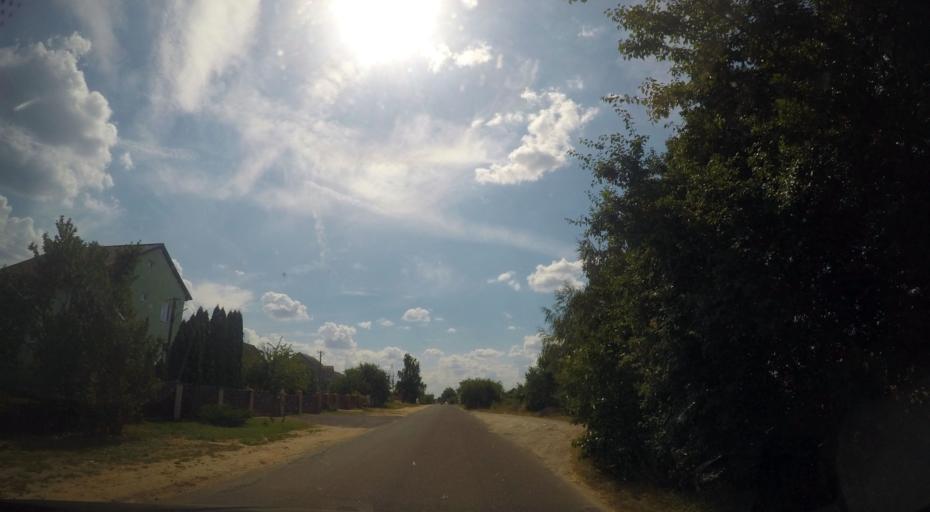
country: BY
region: Grodnenskaya
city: Hrodna
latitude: 53.6350
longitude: 23.8463
